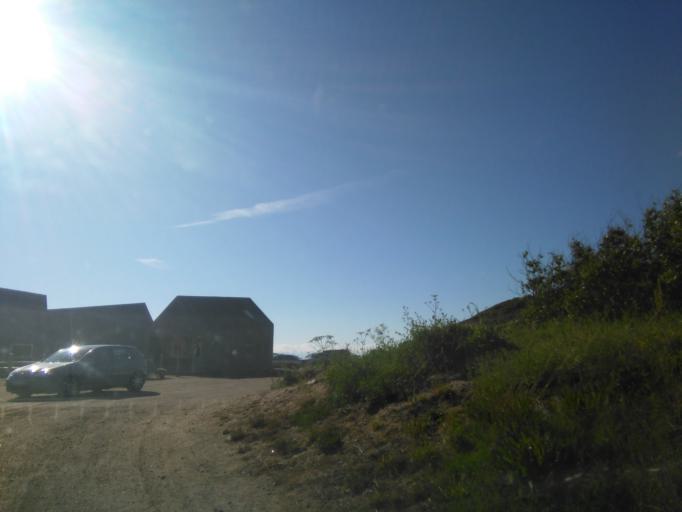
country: DK
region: Capital Region
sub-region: Bornholm Kommune
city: Ronne
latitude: 55.2792
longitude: 14.7561
